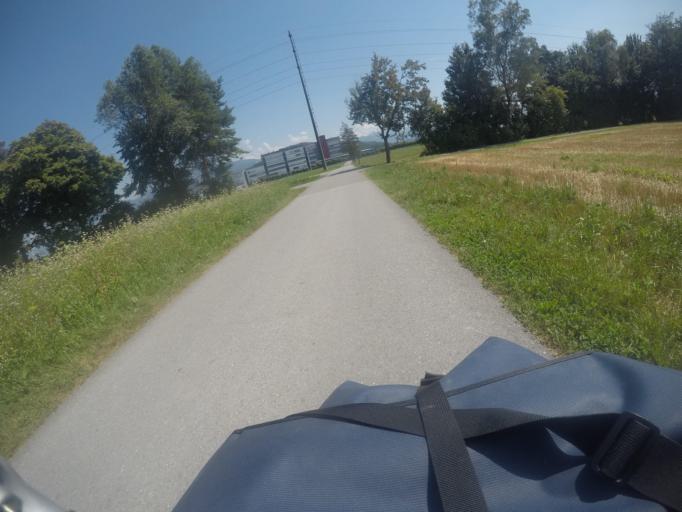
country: AT
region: Vorarlberg
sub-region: Politischer Bezirk Feldkirch
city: Koblach
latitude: 47.3481
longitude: 9.5864
